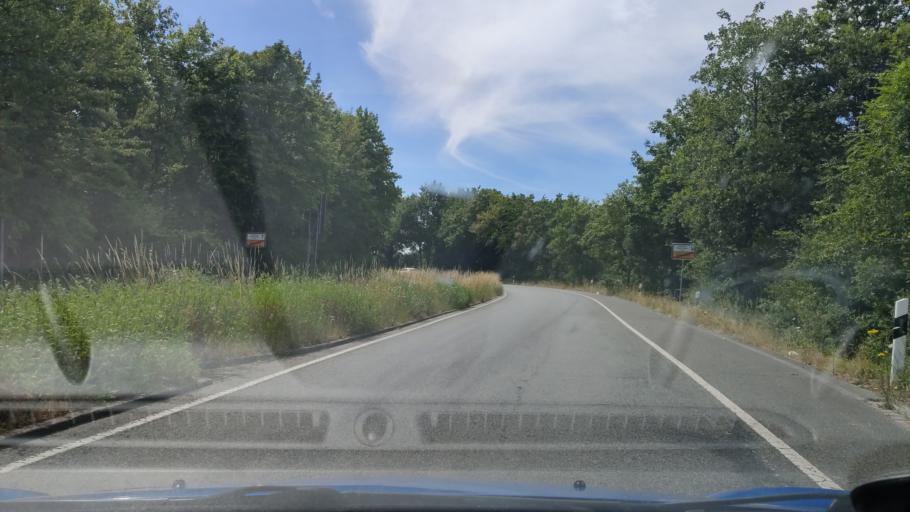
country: DE
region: Lower Saxony
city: Ronnenberg
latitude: 52.3486
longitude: 9.6891
